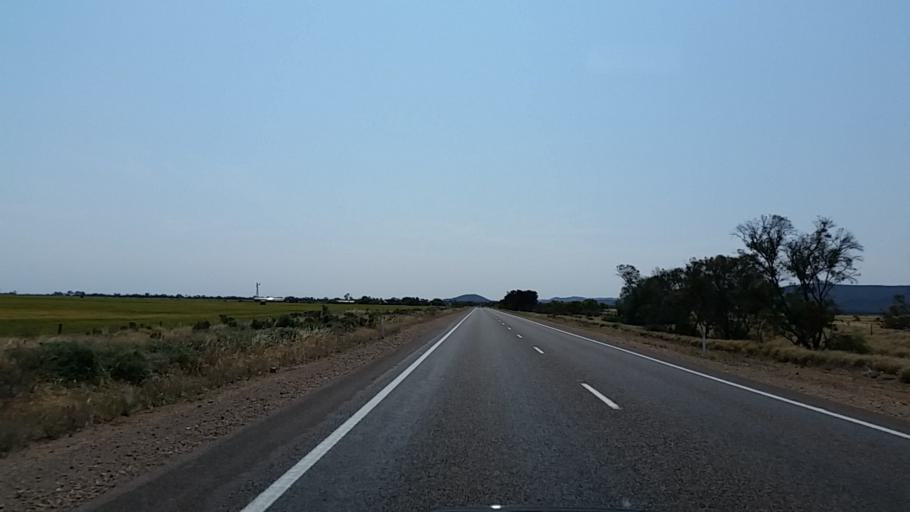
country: AU
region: South Australia
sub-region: Port Pirie City and Dists
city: Port Pirie
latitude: -32.8835
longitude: 137.9823
